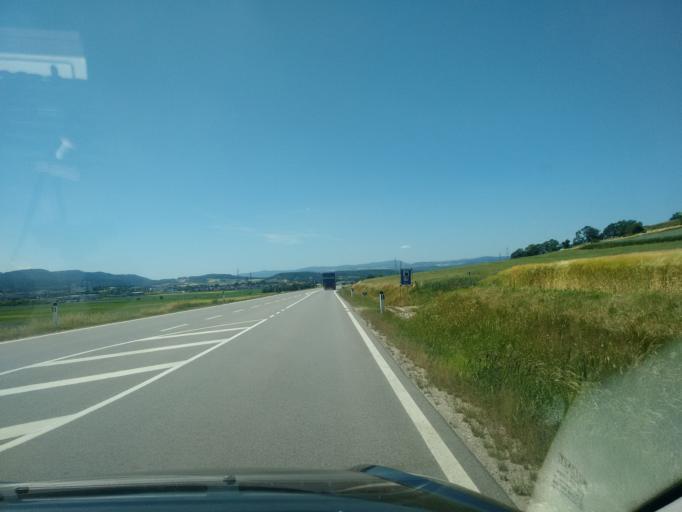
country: AT
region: Lower Austria
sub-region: Politischer Bezirk Sankt Polten
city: Haunoldstein
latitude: 48.1932
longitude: 15.4316
